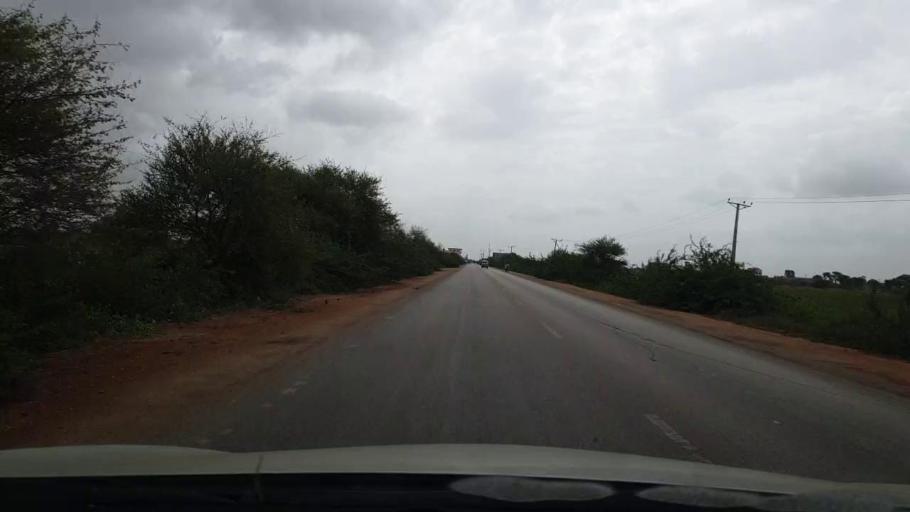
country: PK
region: Sindh
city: Mirpur Batoro
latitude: 24.6170
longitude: 68.2902
